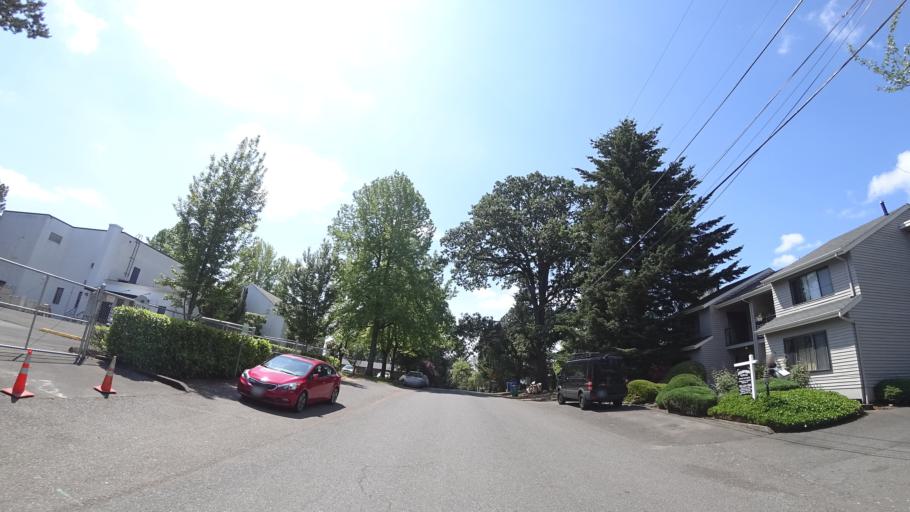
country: US
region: Oregon
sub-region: Washington County
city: Garden Home-Whitford
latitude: 45.4683
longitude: -122.7052
